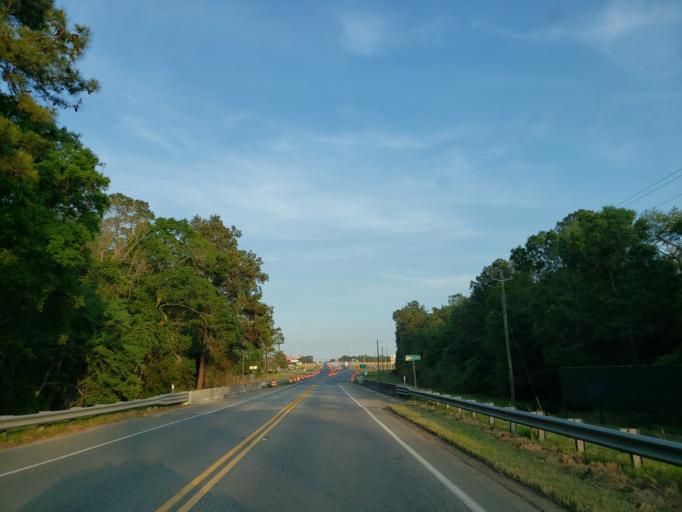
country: US
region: Georgia
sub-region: Lowndes County
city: Hahira
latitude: 30.9940
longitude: -83.3942
